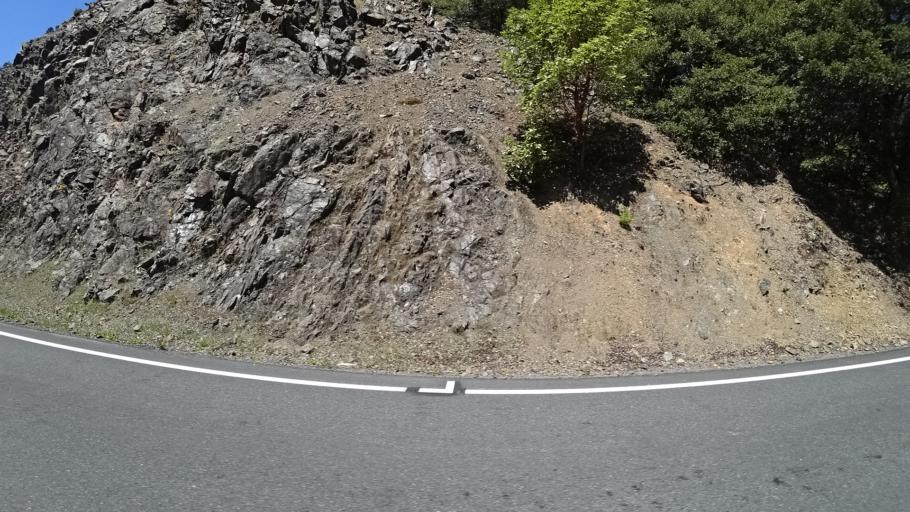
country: US
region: California
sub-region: Humboldt County
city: Willow Creek
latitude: 40.9250
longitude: -123.6894
